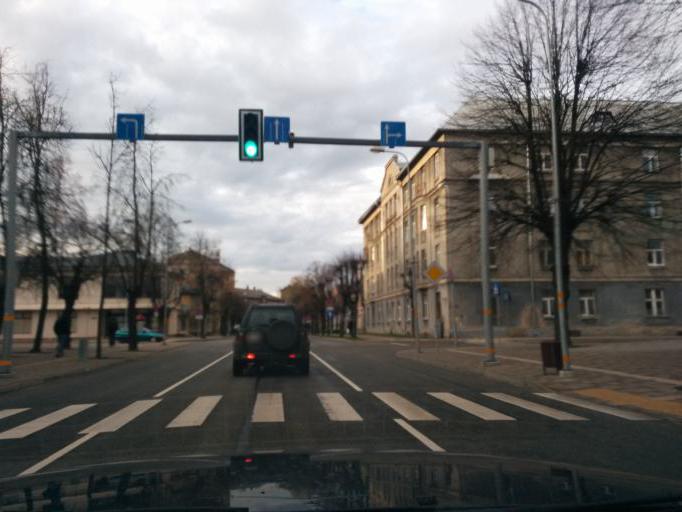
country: LV
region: Jelgava
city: Jelgava
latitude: 56.6444
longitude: 23.7309
